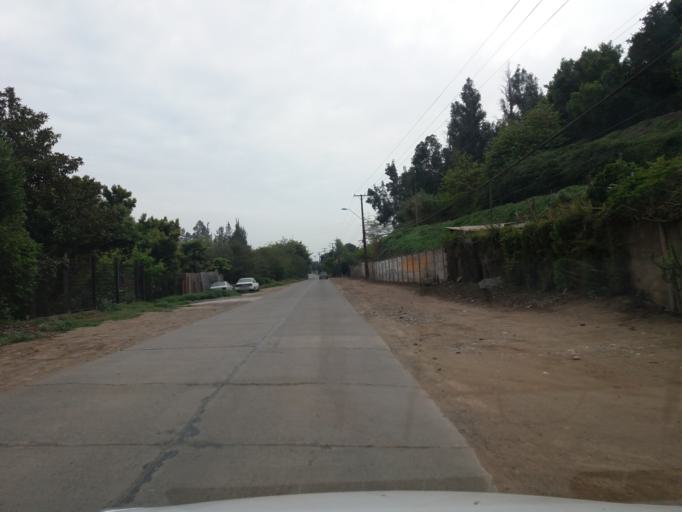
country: CL
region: Valparaiso
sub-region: Provincia de Quillota
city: Hacienda La Calera
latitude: -32.8262
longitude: -71.1276
